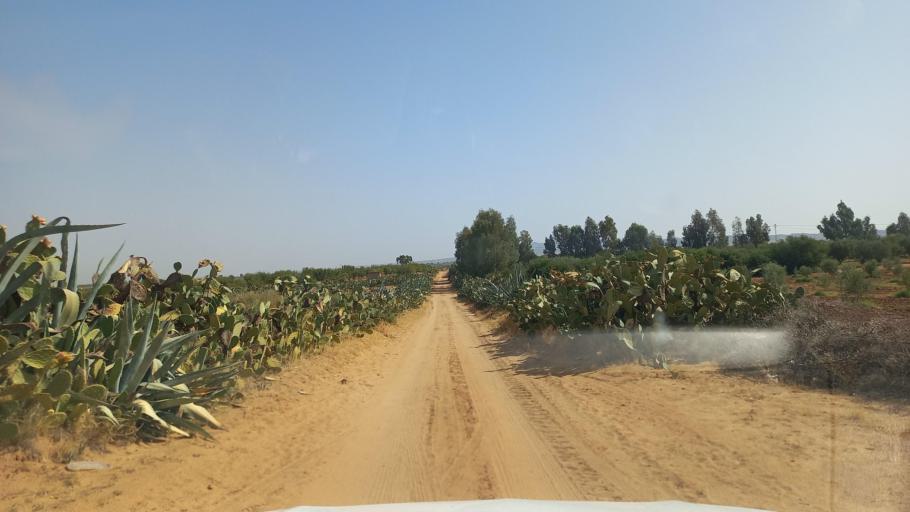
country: TN
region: Al Qasrayn
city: Kasserine
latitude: 35.2324
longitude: 9.0522
